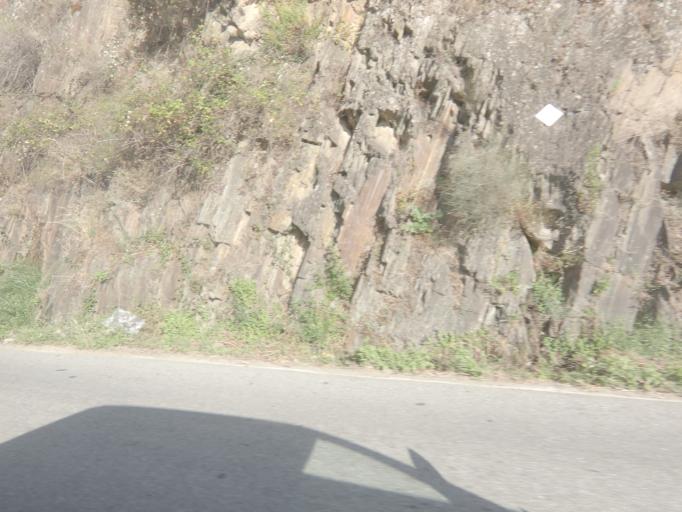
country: PT
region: Viseu
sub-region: Tabuaco
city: Tabuaco
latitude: 41.1678
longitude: -7.5601
